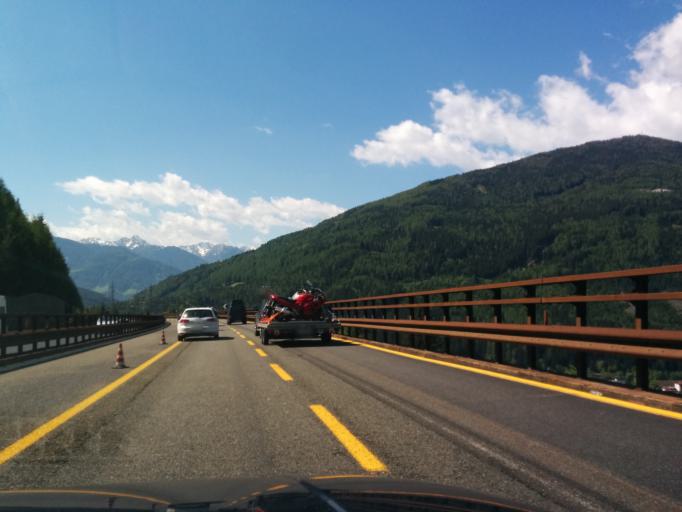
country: IT
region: Trentino-Alto Adige
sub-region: Bolzano
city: Colle Isarco
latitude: 46.9434
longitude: 11.4504
